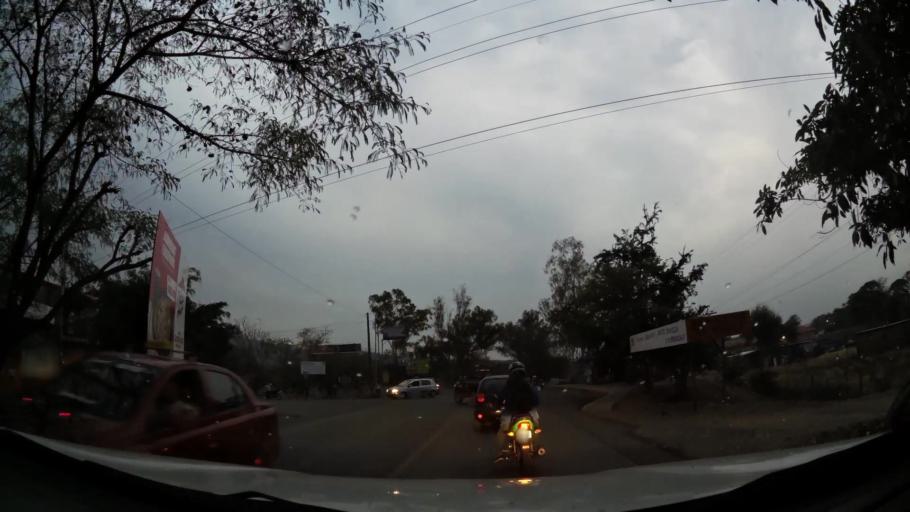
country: NI
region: Esteli
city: Esteli
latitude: 13.1074
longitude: -86.3577
